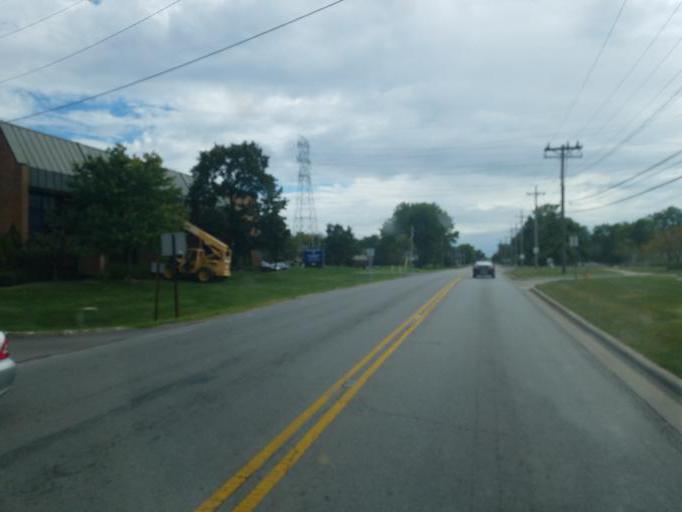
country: US
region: Ohio
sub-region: Franklin County
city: Reynoldsburg
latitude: 39.9797
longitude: -82.8362
